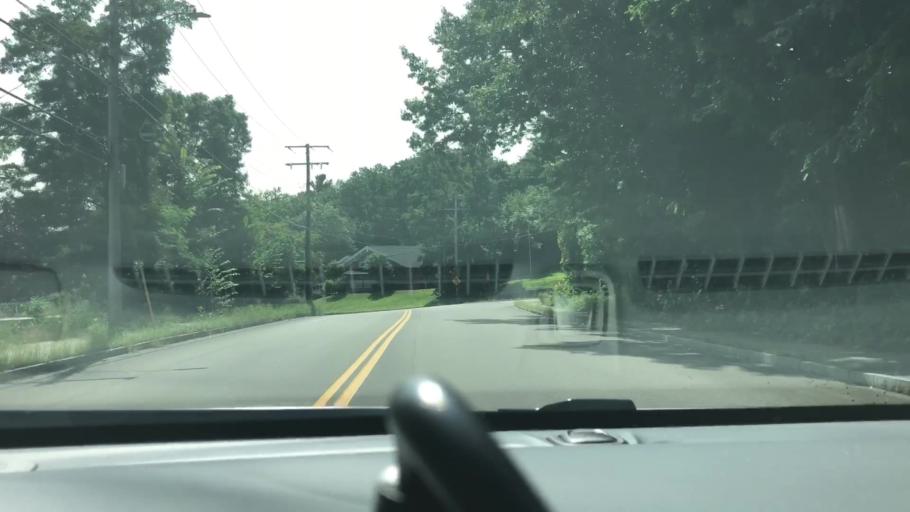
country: US
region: New Hampshire
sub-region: Hillsborough County
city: Pinardville
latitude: 42.9811
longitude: -71.4853
